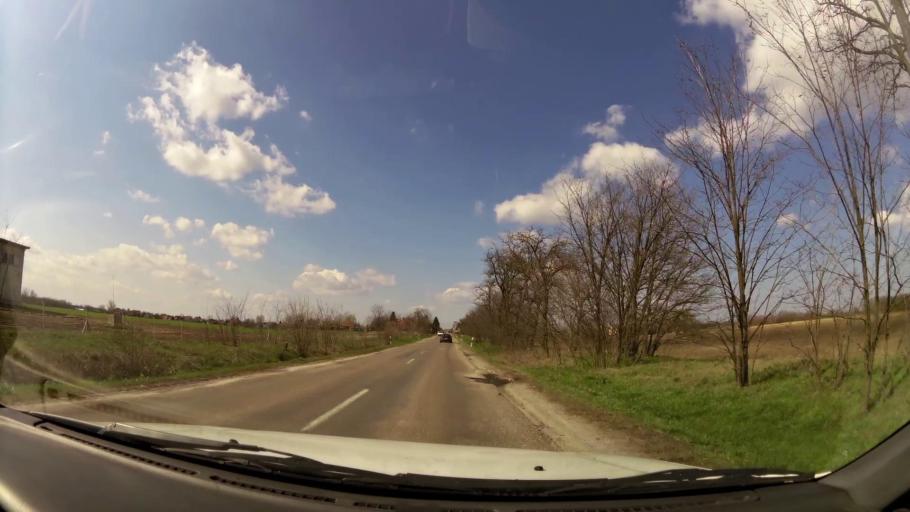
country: HU
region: Pest
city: Farmos
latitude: 47.3521
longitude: 19.8573
